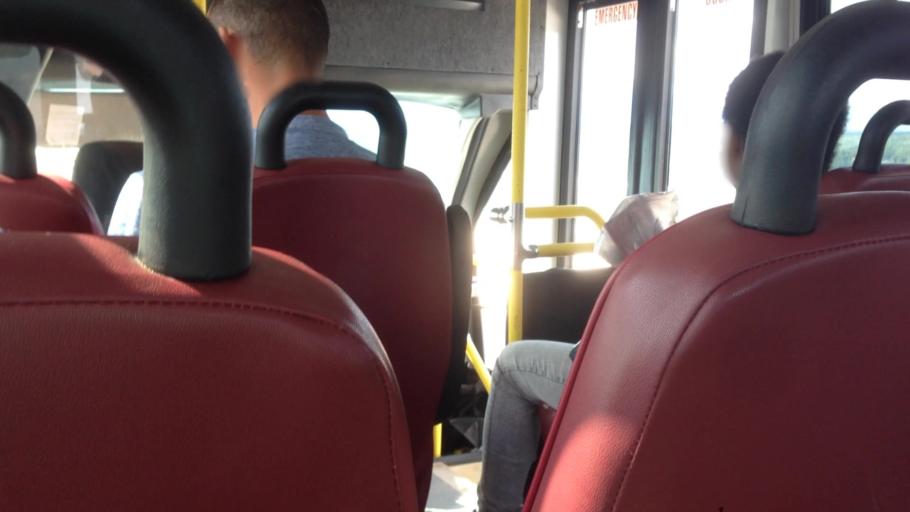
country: US
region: New York
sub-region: Ulster County
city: Lake Katrine
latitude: 41.9770
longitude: -73.9439
